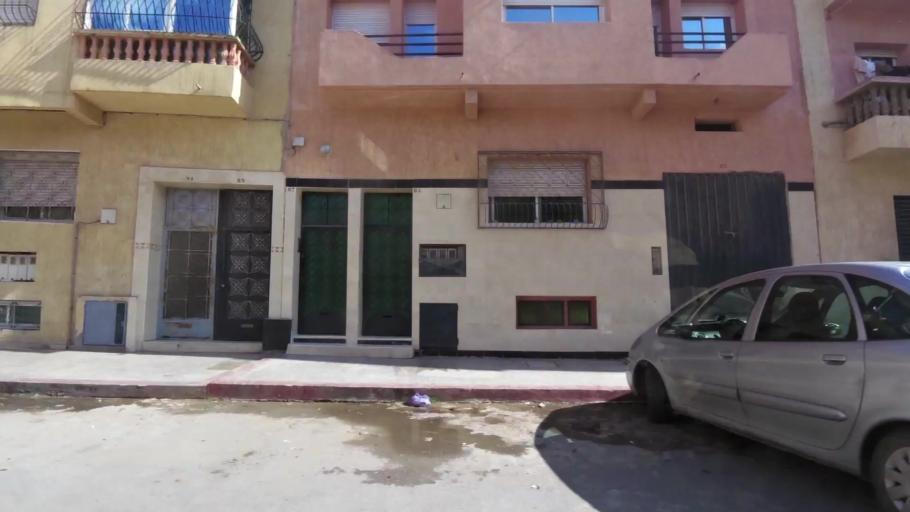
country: MA
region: Chaouia-Ouardigha
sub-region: Settat Province
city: Berrechid
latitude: 33.2579
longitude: -7.5719
